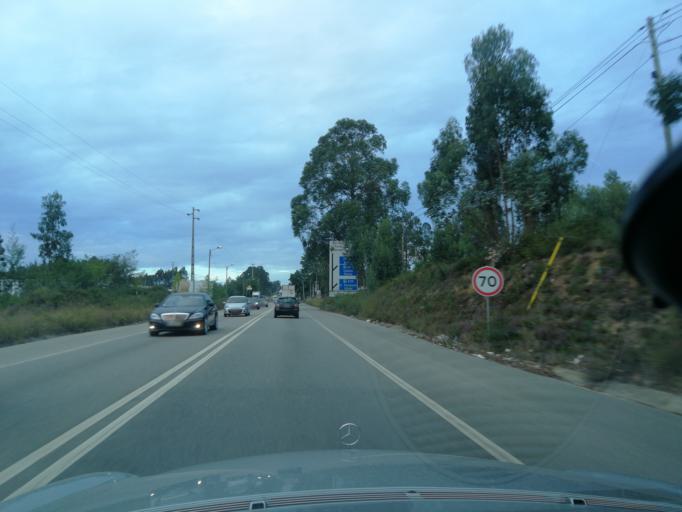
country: PT
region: Aveiro
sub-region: Albergaria-A-Velha
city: Albergaria-a-Velha
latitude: 40.6679
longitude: -8.4747
